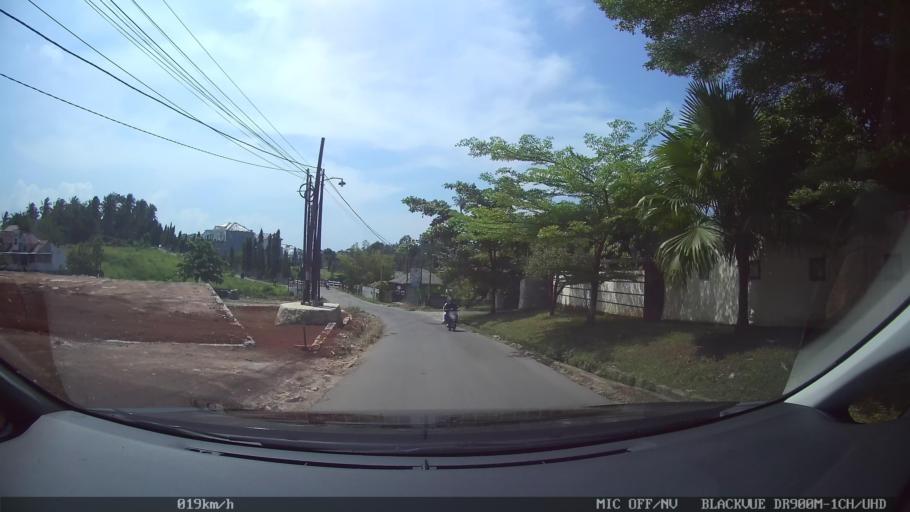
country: ID
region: Lampung
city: Kedaton
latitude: -5.3707
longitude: 105.2592
